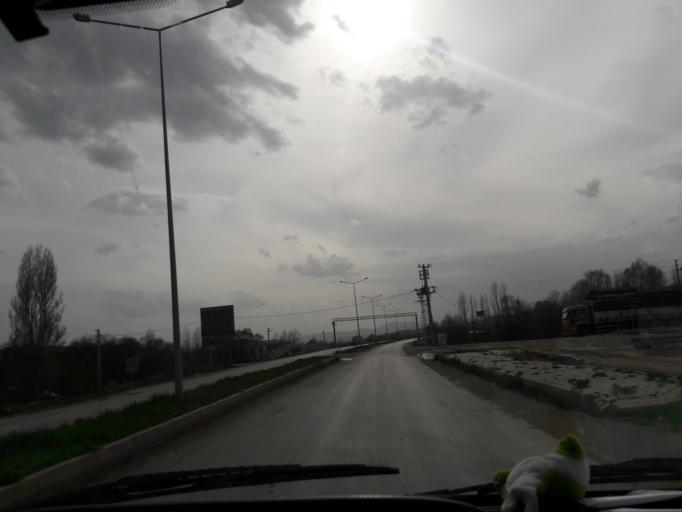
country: TR
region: Gumushane
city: Siran
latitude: 40.1774
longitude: 39.1095
